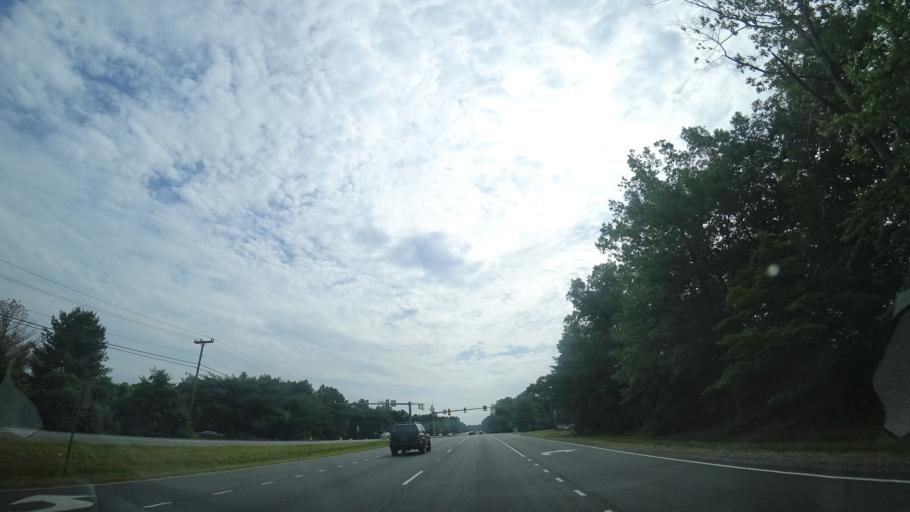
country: US
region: Virginia
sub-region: Spotsylvania County
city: Spotsylvania
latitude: 38.2374
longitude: -77.5487
